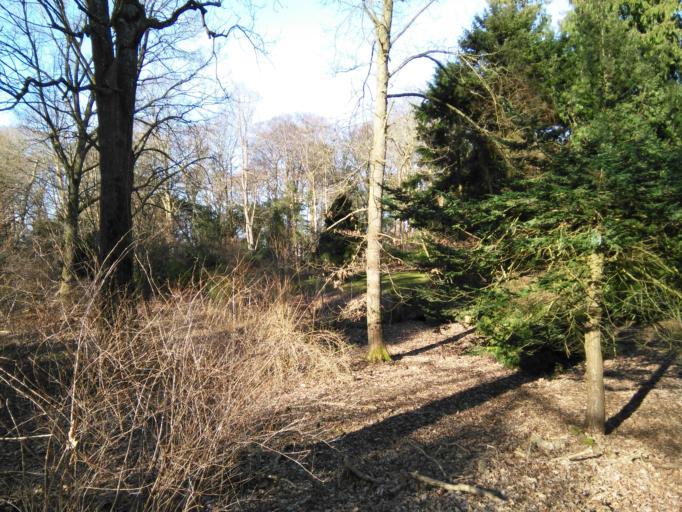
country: DK
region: Central Jutland
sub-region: Arhus Kommune
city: Arhus
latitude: 56.1254
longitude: 10.2030
